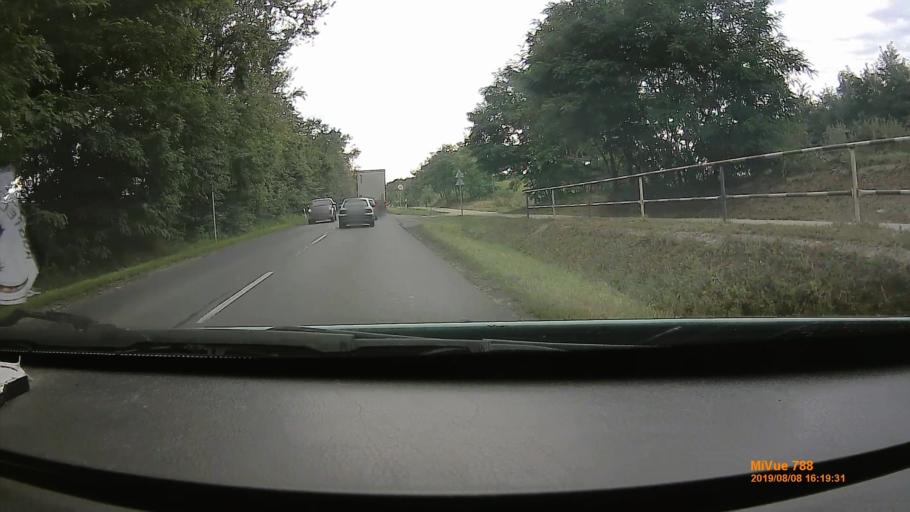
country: HU
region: Szabolcs-Szatmar-Bereg
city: Mateszalka
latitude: 47.9661
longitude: 22.2748
